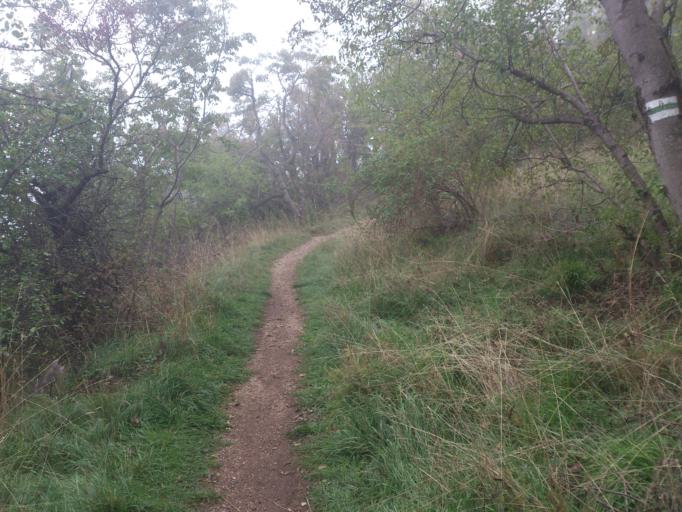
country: HU
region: Pest
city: Pilisszanto
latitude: 47.6833
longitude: 18.8747
